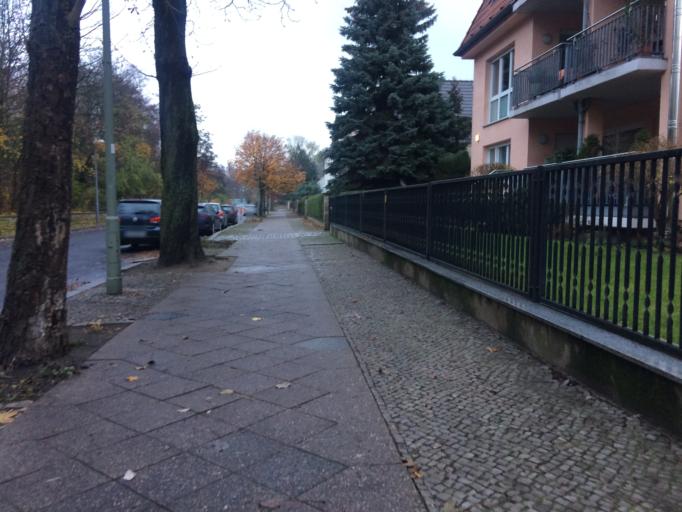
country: DE
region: Berlin
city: Fennpfuhl
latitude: 52.5341
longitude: 13.4584
